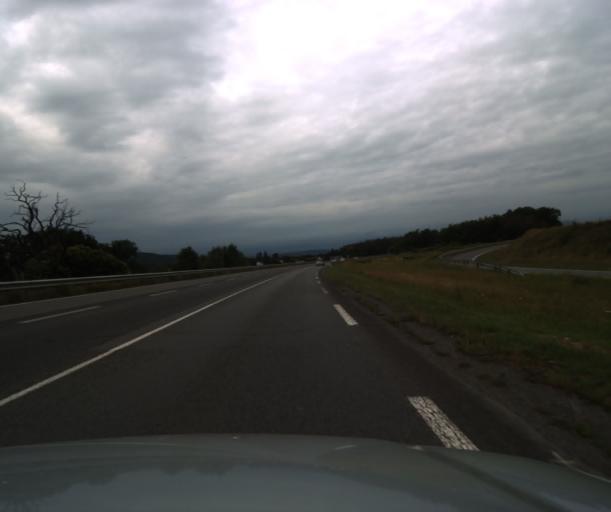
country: FR
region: Midi-Pyrenees
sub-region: Departement des Hautes-Pyrenees
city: Juillan
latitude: 43.1943
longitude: 0.0105
